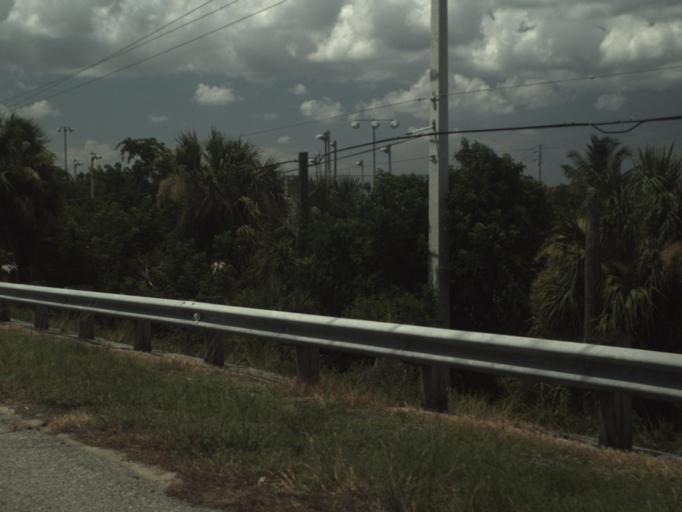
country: US
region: Florida
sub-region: Martin County
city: Hobe Sound
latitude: 27.0532
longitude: -80.1320
